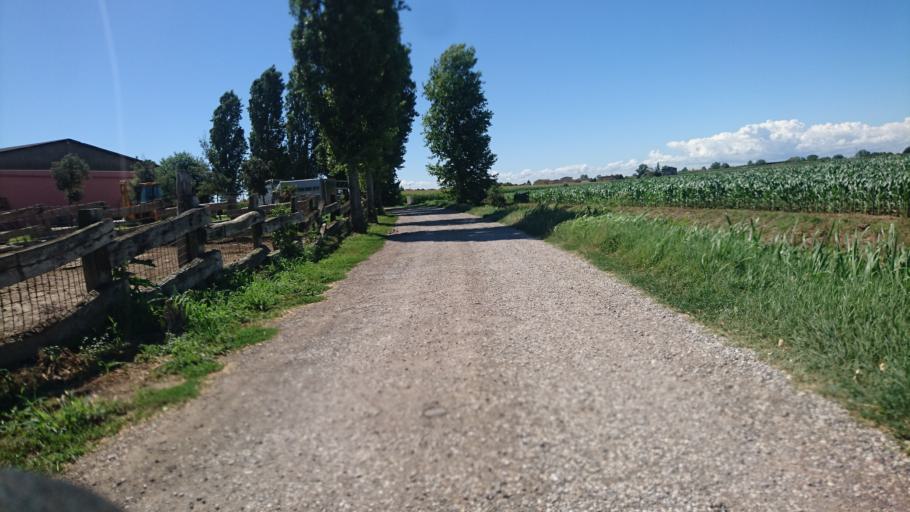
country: IT
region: Veneto
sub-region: Provincia di Padova
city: Pontelongo
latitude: 45.2581
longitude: 12.0160
